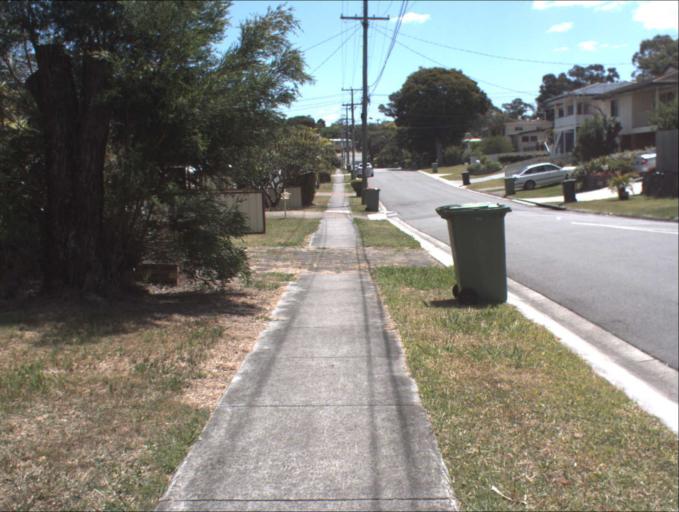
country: AU
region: Queensland
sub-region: Logan
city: Rochedale South
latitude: -27.5999
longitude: 153.1141
